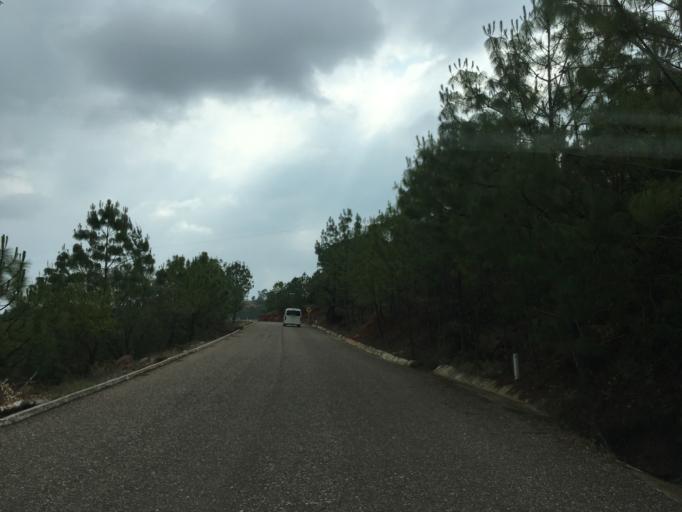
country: MX
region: Oaxaca
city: Santiago Tilantongo
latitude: 17.2432
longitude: -97.3058
